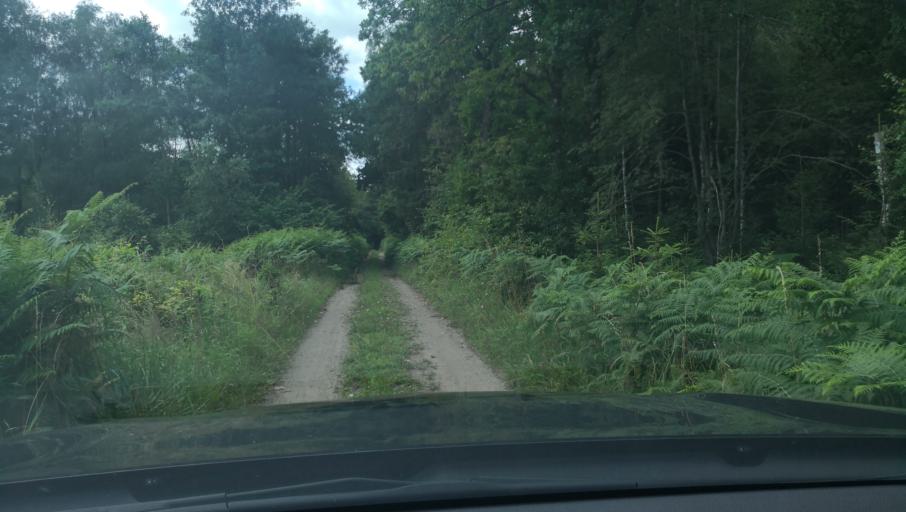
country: SE
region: Skane
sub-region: Simrishamns Kommun
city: Kivik
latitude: 55.6188
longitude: 14.1096
